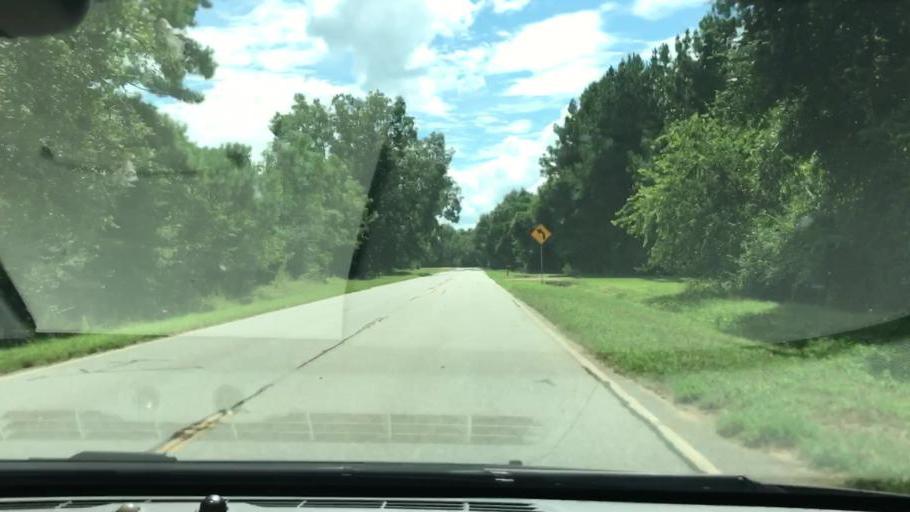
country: US
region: Georgia
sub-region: Quitman County
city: Georgetown
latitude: 32.0492
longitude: -85.0366
